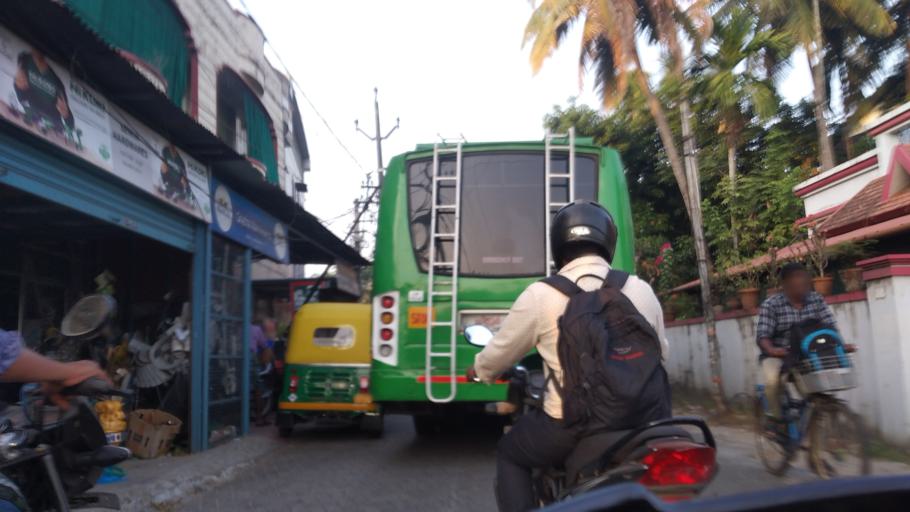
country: IN
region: Kerala
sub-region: Ernakulam
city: Elur
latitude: 10.0294
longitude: 76.2753
